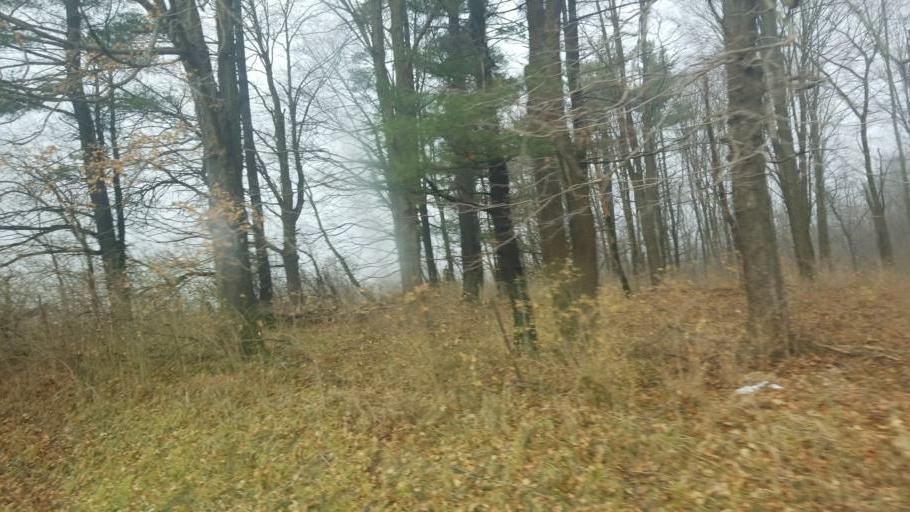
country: US
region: Ohio
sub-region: Champaign County
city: North Lewisburg
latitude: 40.2860
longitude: -83.6154
